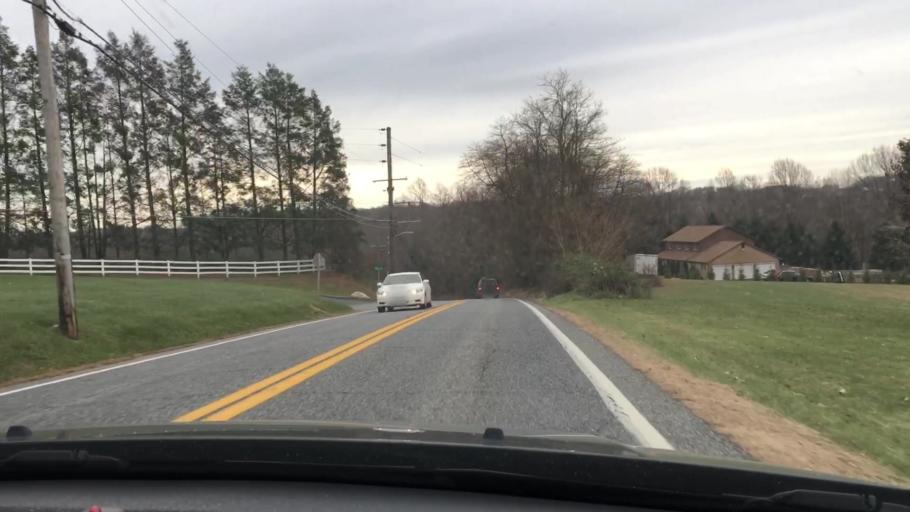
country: US
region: Maryland
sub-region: Harford County
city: Aberdeen
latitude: 39.5965
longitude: -76.1904
